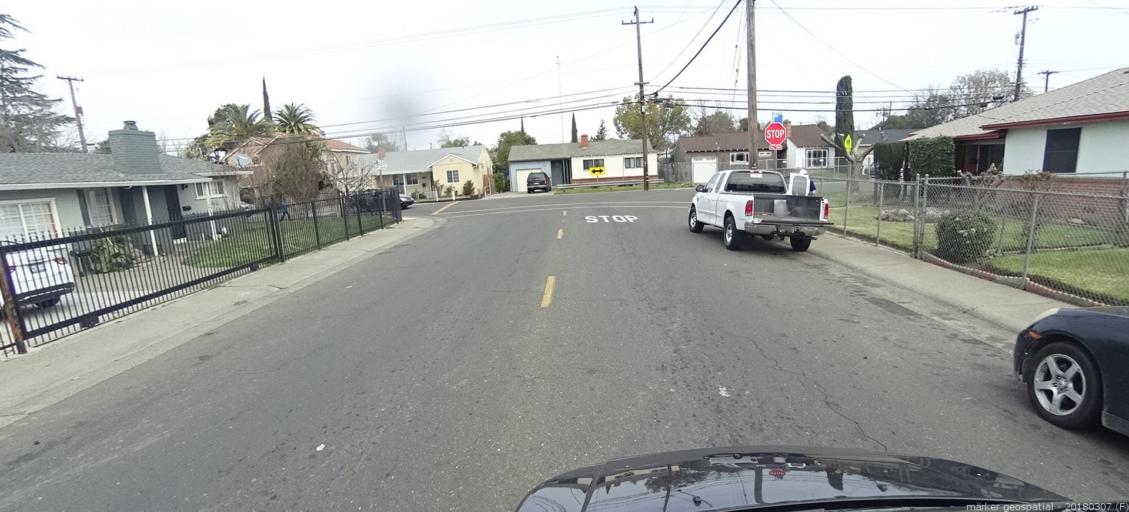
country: US
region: California
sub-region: Sacramento County
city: Parkway
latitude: 38.5318
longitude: -121.4563
